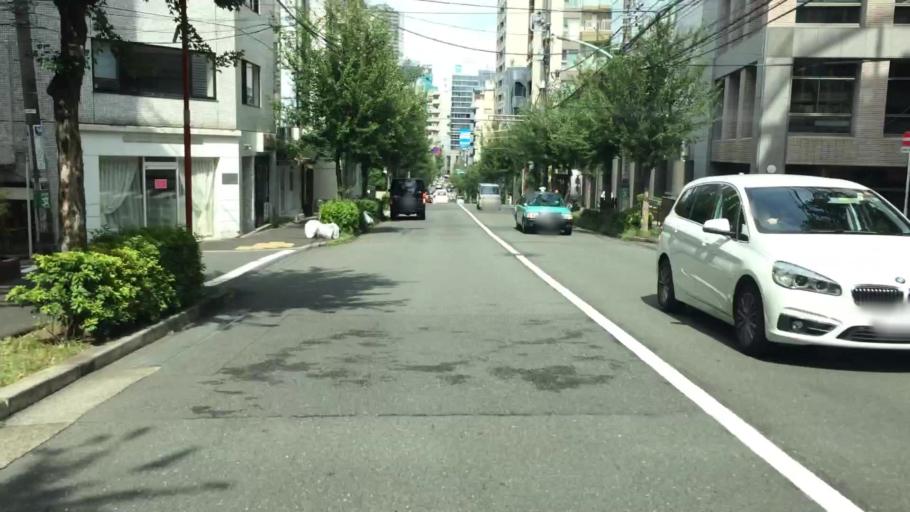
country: JP
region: Tokyo
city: Tokyo
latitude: 35.6443
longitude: 139.7093
